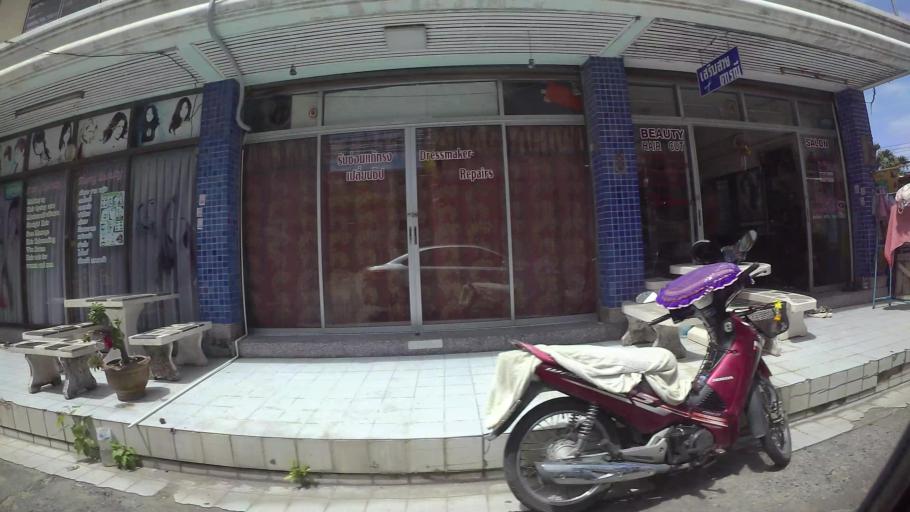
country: TH
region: Chon Buri
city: Phatthaya
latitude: 12.9339
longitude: 100.8906
